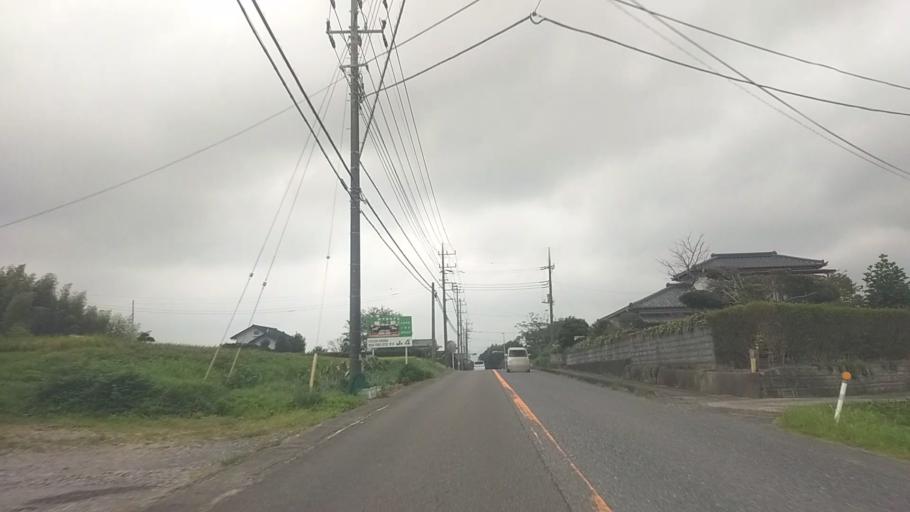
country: JP
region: Chiba
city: Kawaguchi
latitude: 35.1159
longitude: 140.0780
